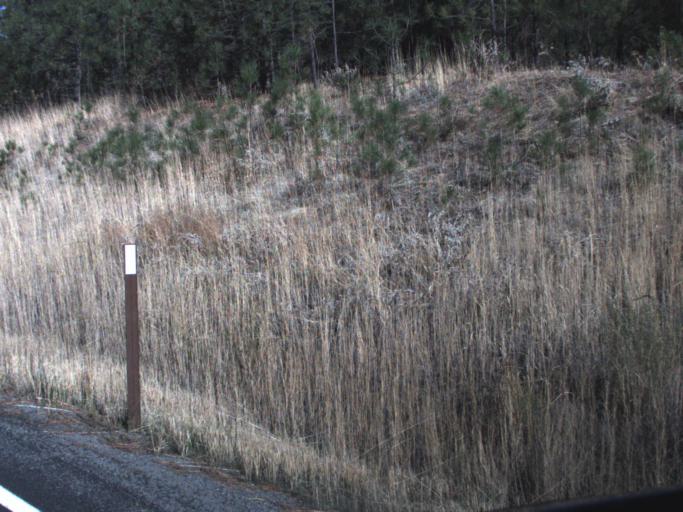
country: US
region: Washington
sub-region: Lincoln County
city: Davenport
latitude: 48.0318
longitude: -118.2313
